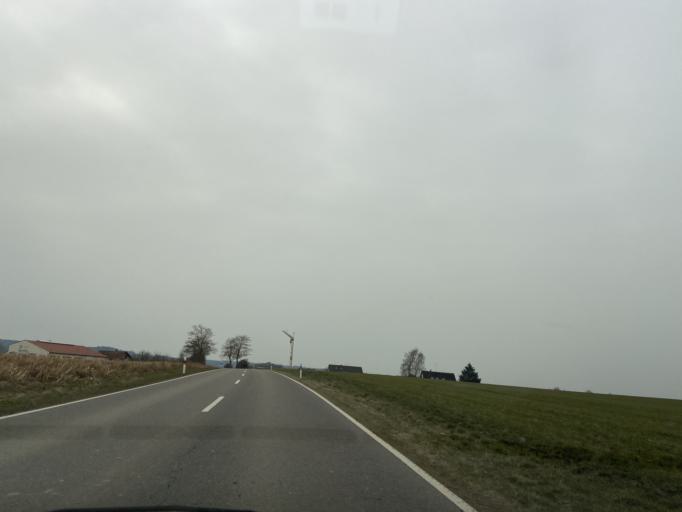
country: DE
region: Baden-Wuerttemberg
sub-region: Tuebingen Region
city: Ostrach
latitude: 47.9355
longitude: 9.3620
